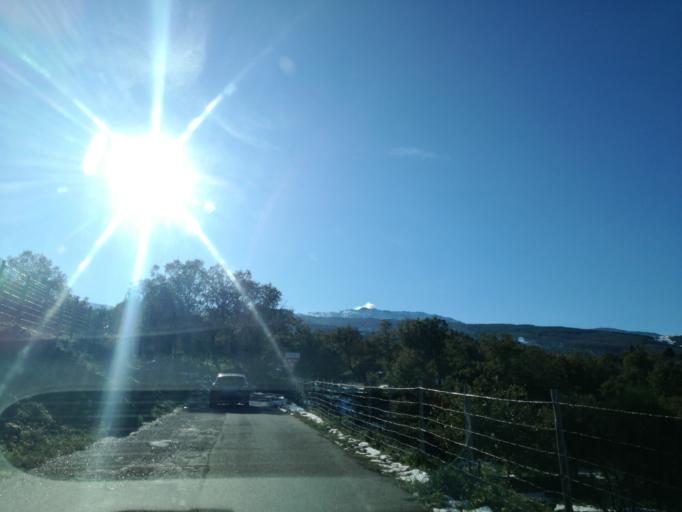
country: IT
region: Sicily
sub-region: Catania
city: Randazzo
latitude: 37.8570
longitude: 14.9839
